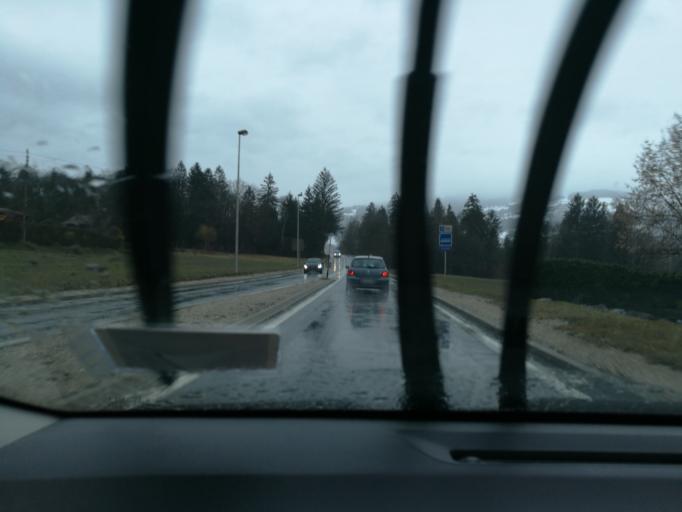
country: FR
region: Rhone-Alpes
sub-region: Departement de la Haute-Savoie
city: Domancy
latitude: 45.9289
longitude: 6.6551
